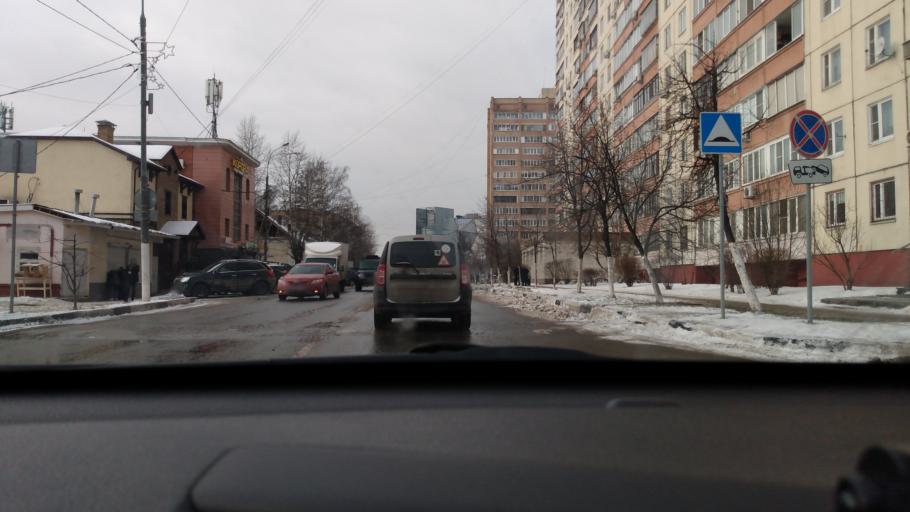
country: RU
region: Moskovskaya
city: Zheleznodorozhnyy
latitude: 55.7475
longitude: 38.0124
